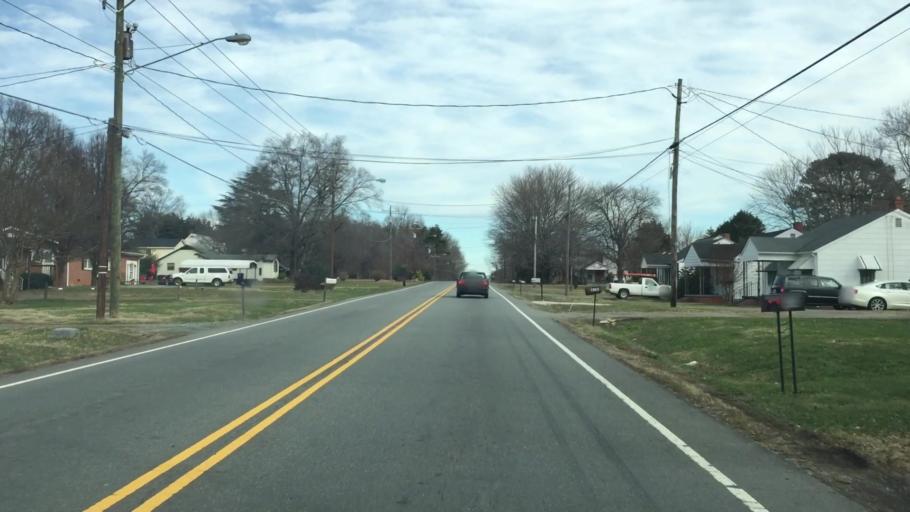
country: US
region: North Carolina
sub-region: Forsyth County
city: Walkertown
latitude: 36.1264
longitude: -80.1761
